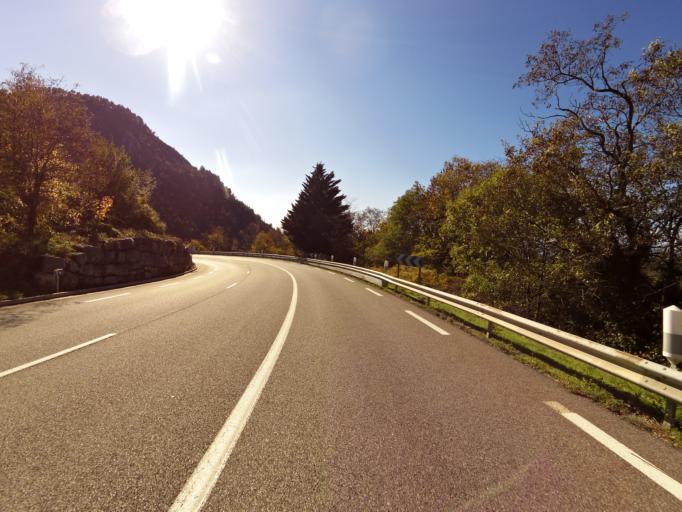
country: FR
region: Rhone-Alpes
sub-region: Departement de l'Ardeche
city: Saint-Priest
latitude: 44.7100
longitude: 4.4879
